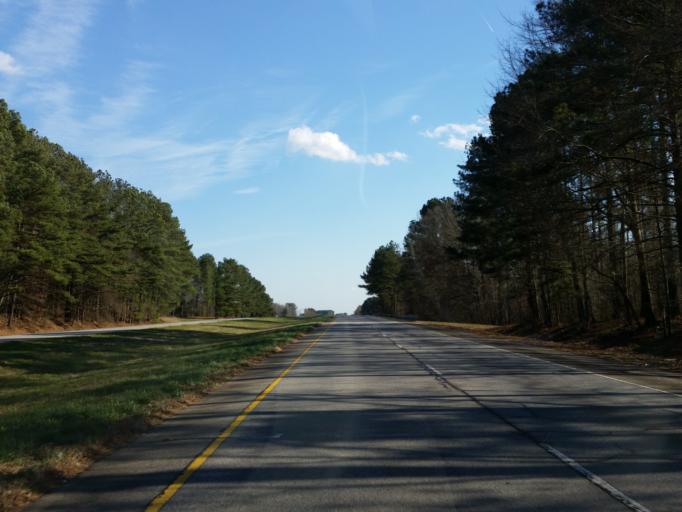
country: US
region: Georgia
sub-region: Spalding County
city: Griffin
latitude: 33.1846
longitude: -84.2739
